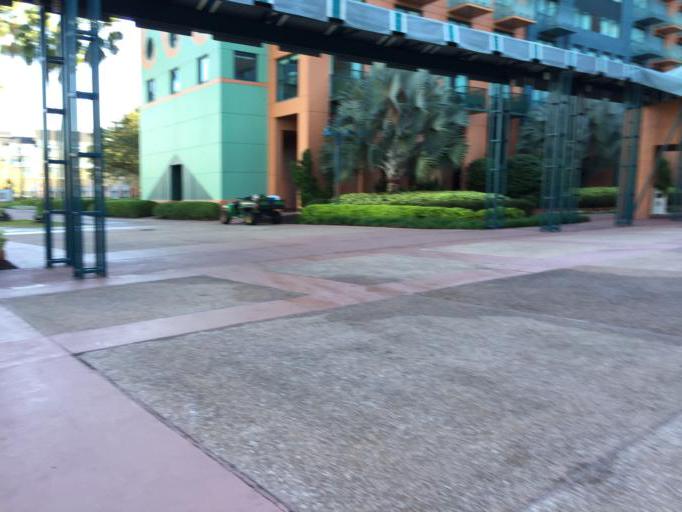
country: US
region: Florida
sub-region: Osceola County
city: Celebration
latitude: 28.3662
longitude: -81.5593
